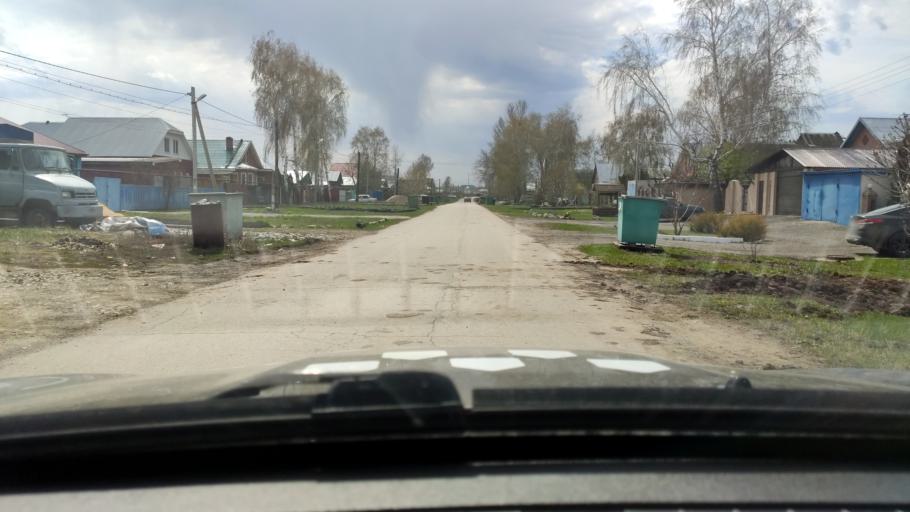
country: RU
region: Samara
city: Tol'yatti
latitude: 53.5600
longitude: 49.3986
